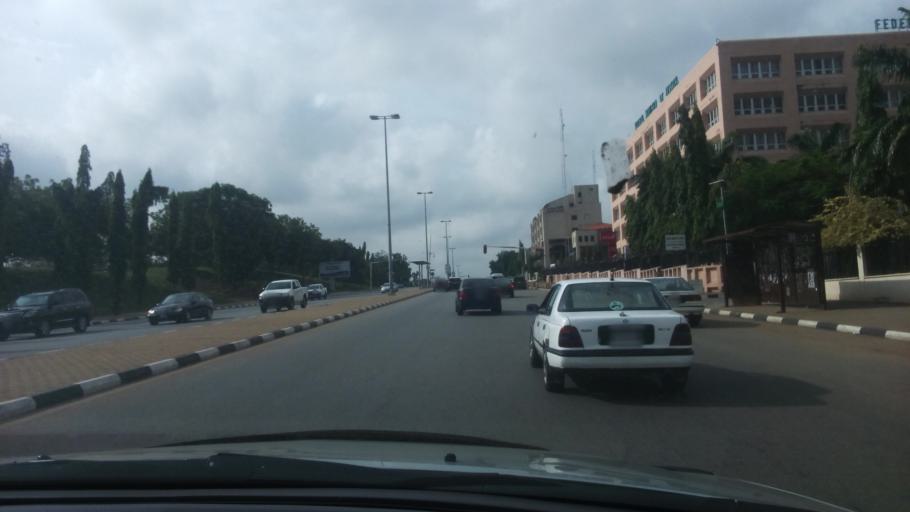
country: NG
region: Abuja Federal Capital Territory
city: Abuja
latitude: 9.0674
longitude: 7.4966
